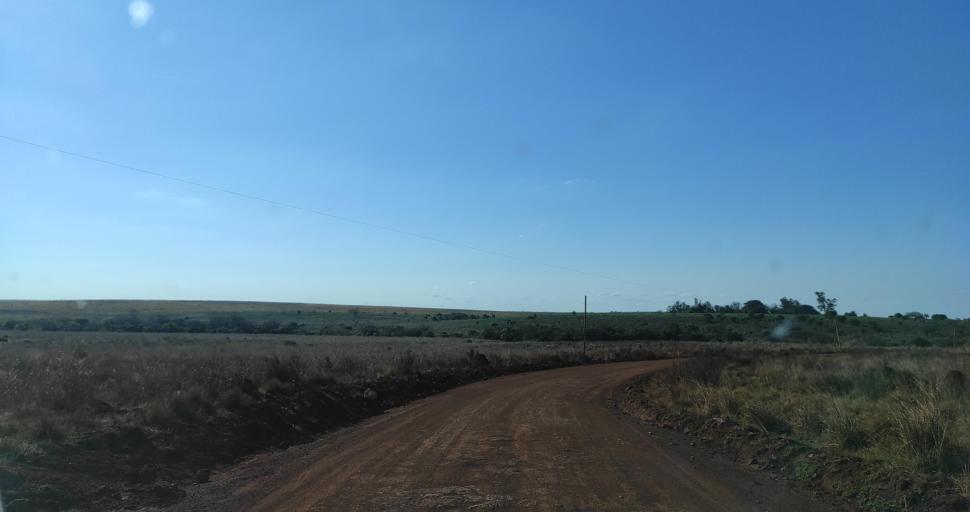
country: PY
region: Itapua
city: San Juan del Parana
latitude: -27.4483
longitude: -56.0645
